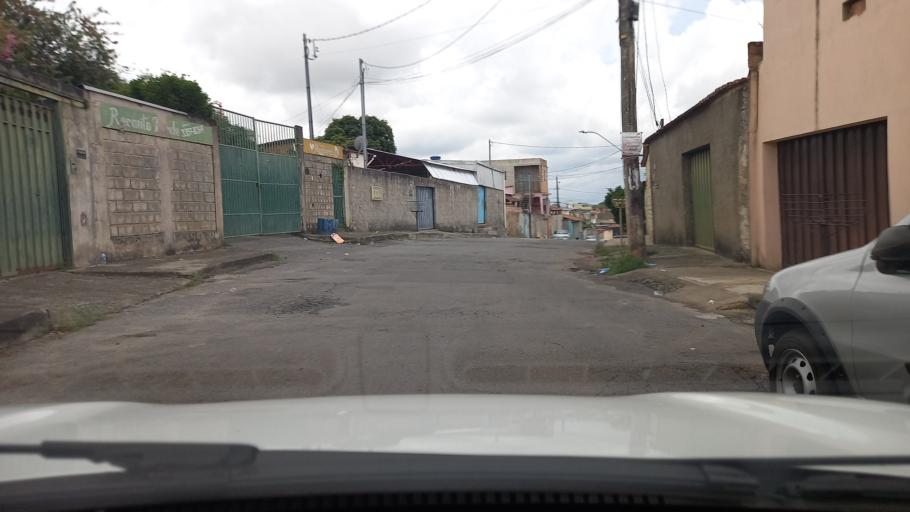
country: BR
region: Minas Gerais
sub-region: Contagem
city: Contagem
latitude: -19.9039
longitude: -44.0259
